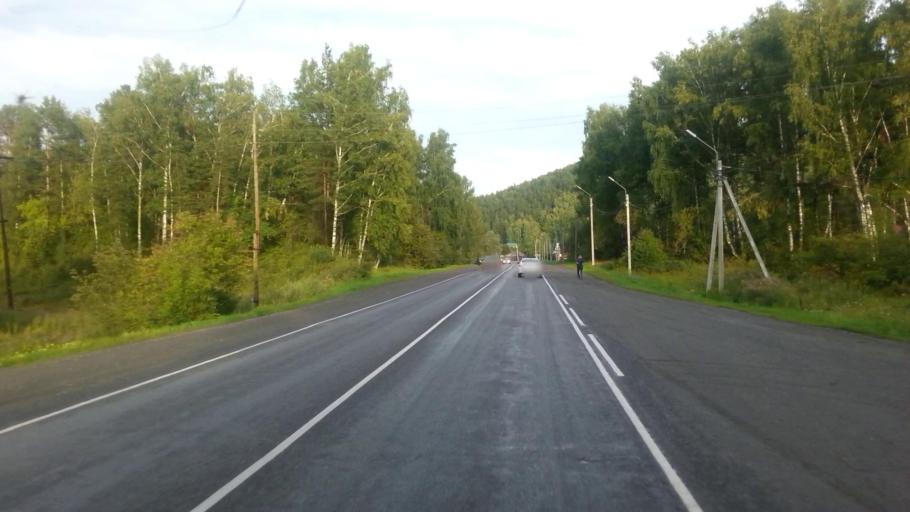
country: RU
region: Altay
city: Souzga
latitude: 51.8857
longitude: 85.8451
